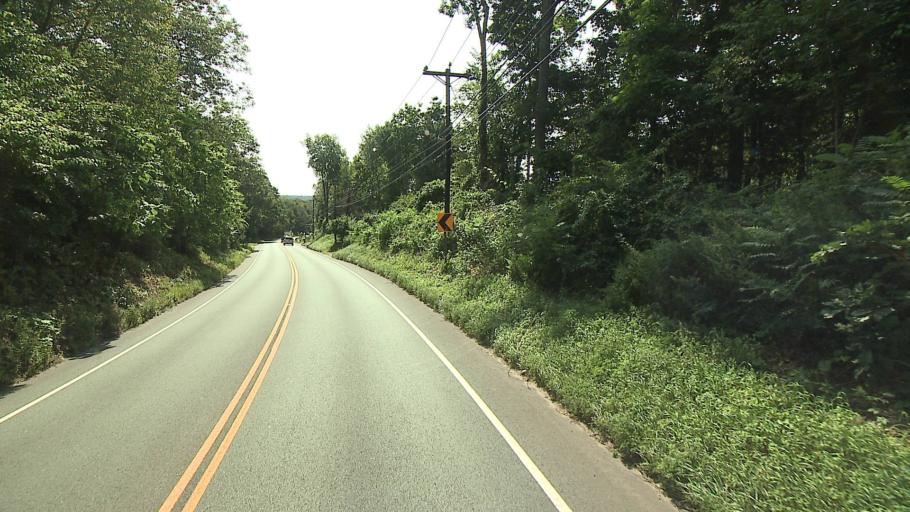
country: US
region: Connecticut
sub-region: Fairfield County
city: Newtown
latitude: 41.3569
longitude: -73.2637
